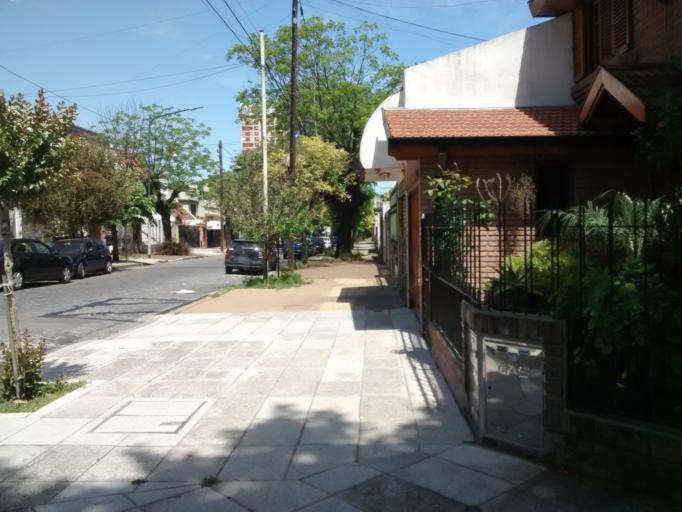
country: AR
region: Buenos Aires
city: Caseros
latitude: -34.6321
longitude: -58.5273
